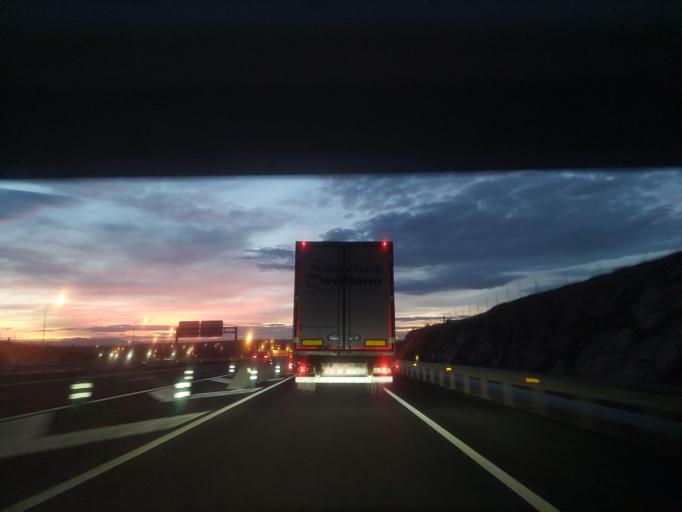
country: ES
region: Castille and Leon
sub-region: Provincia de Segovia
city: Segovia
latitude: 40.9213
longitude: -4.1023
